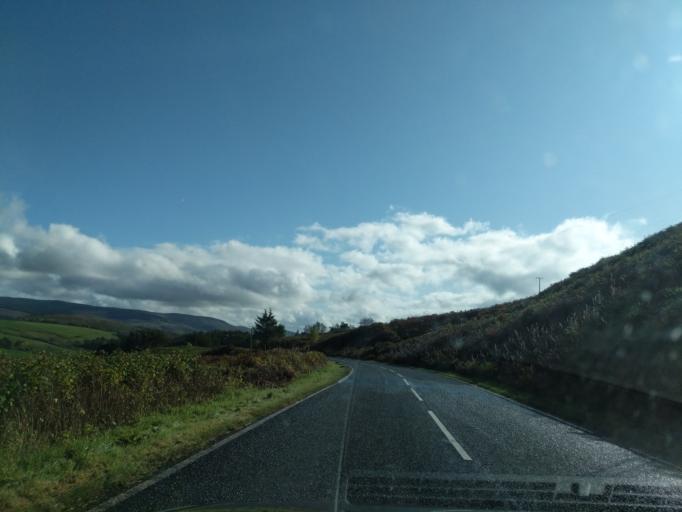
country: GB
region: Scotland
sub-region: Dumfries and Galloway
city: Moffat
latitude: 55.3598
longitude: -3.4751
